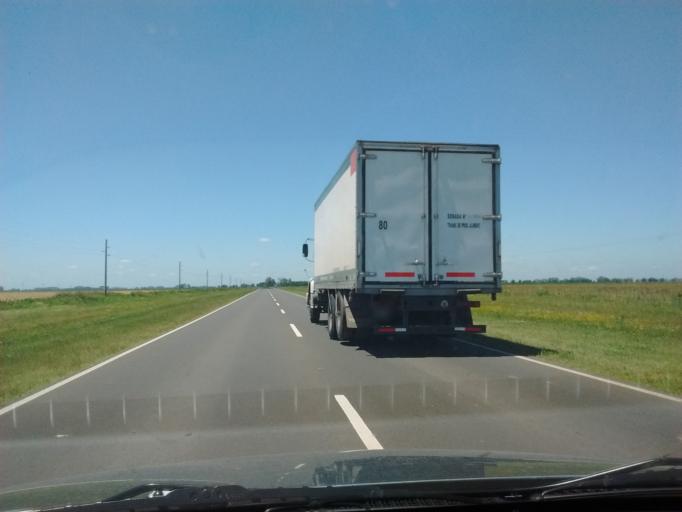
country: AR
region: Entre Rios
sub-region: Departamento de Gualeguay
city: Gualeguay
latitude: -33.0445
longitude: -59.4276
